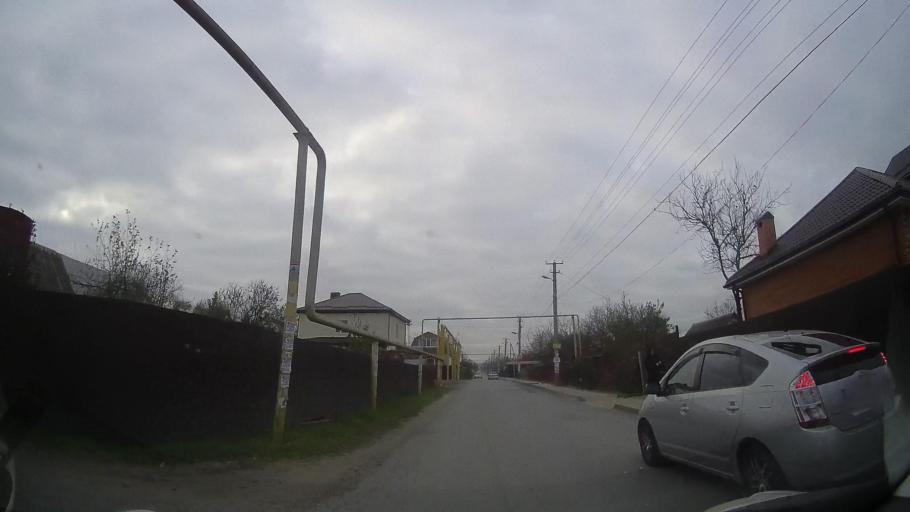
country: RU
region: Rostov
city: Bataysk
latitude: 47.0851
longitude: 39.7611
